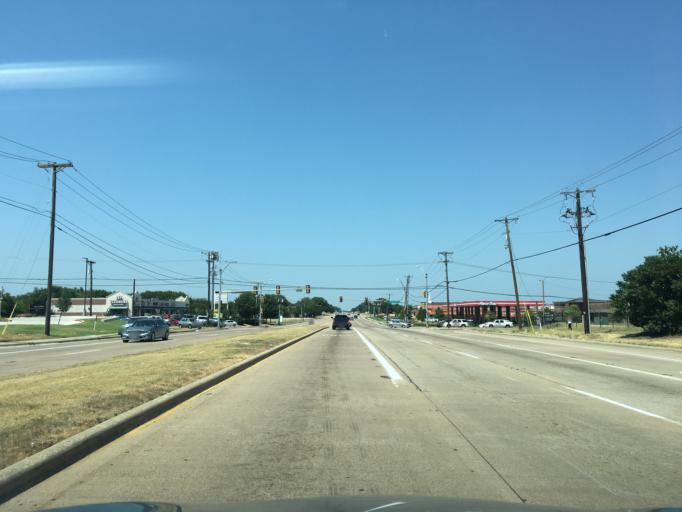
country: US
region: Texas
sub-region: Tarrant County
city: Edgecliff Village
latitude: 32.6338
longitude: -97.3485
